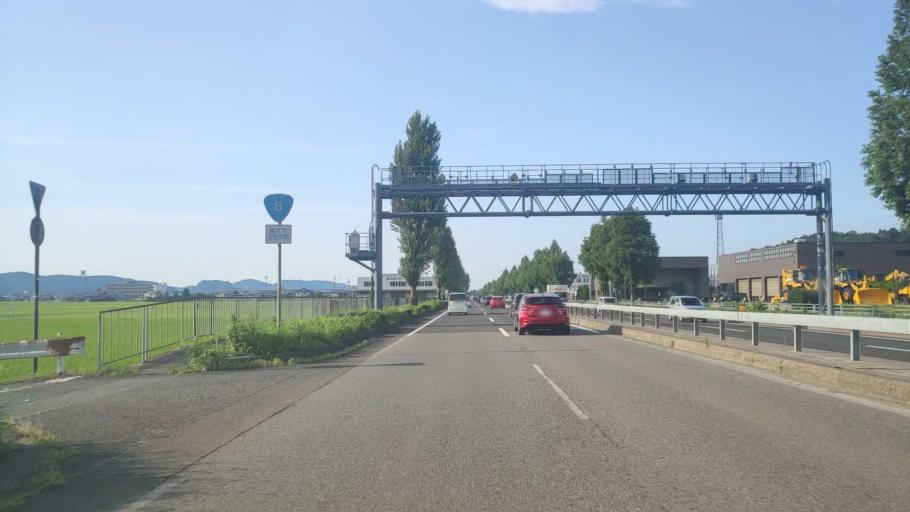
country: JP
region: Fukui
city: Sabae
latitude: 35.9983
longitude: 136.2066
